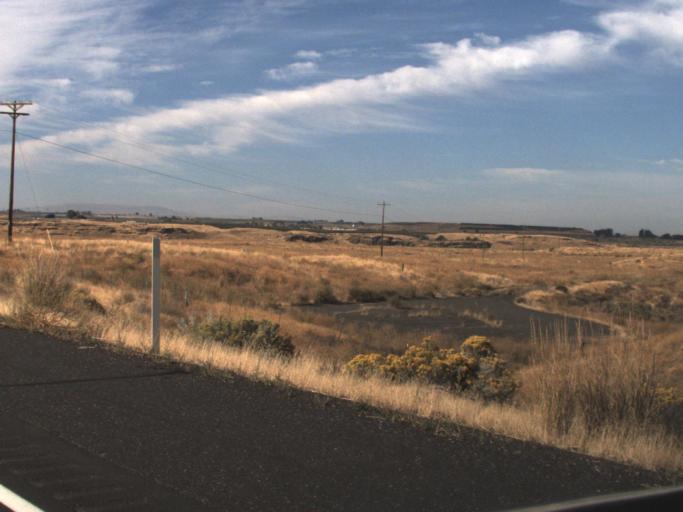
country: US
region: Washington
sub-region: Franklin County
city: Connell
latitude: 46.5715
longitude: -118.9881
